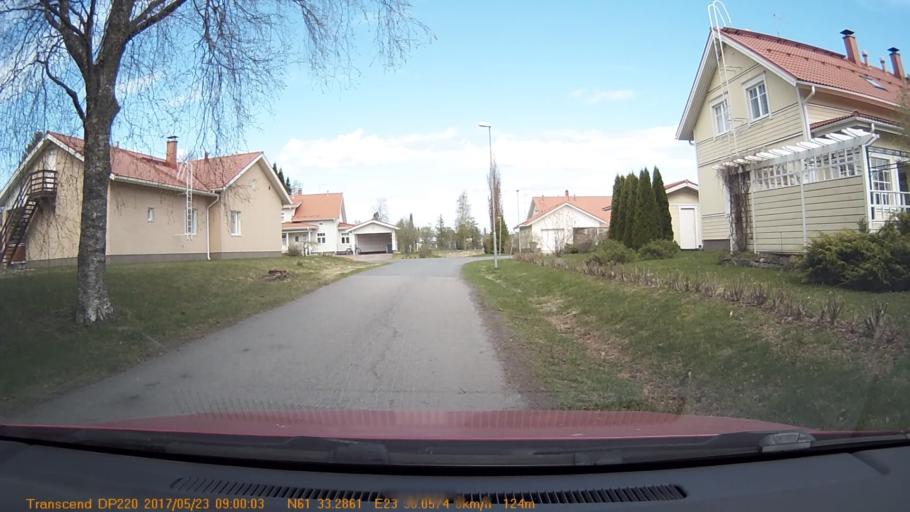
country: FI
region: Pirkanmaa
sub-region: Tampere
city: Yloejaervi
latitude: 61.5548
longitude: 23.6010
